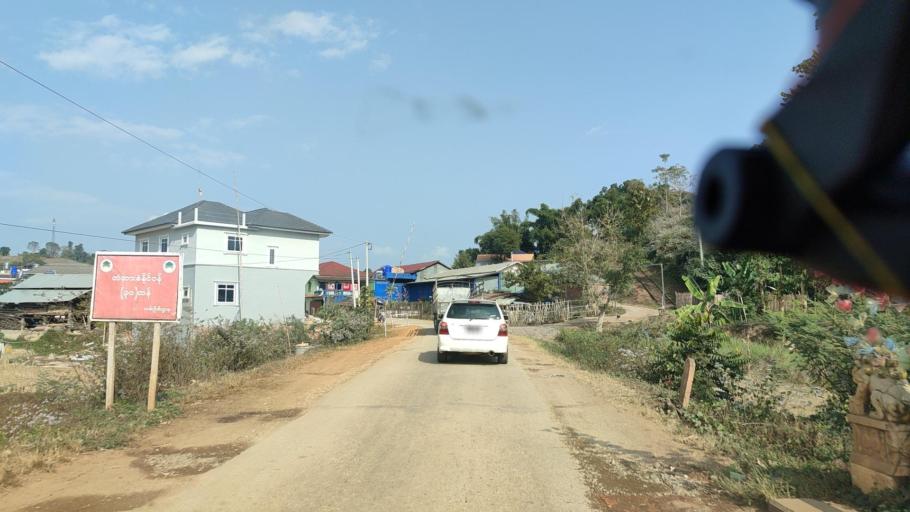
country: CN
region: Yunnan
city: Nayun
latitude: 21.7964
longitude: 99.6376
